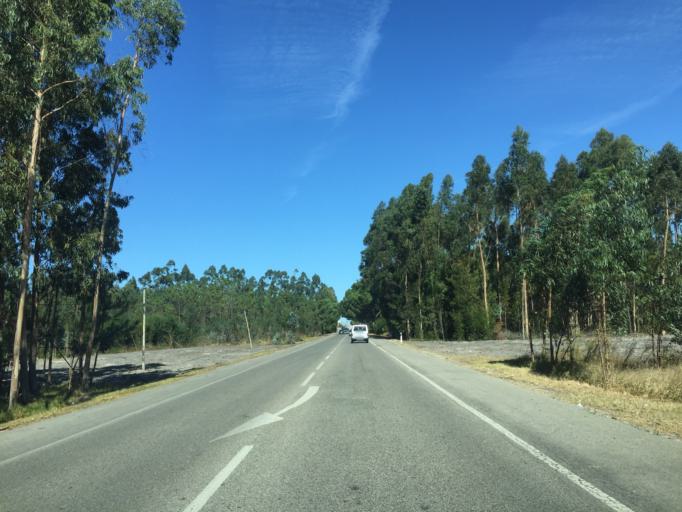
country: PT
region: Coimbra
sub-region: Figueira da Foz
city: Alhadas
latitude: 40.2942
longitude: -8.7639
